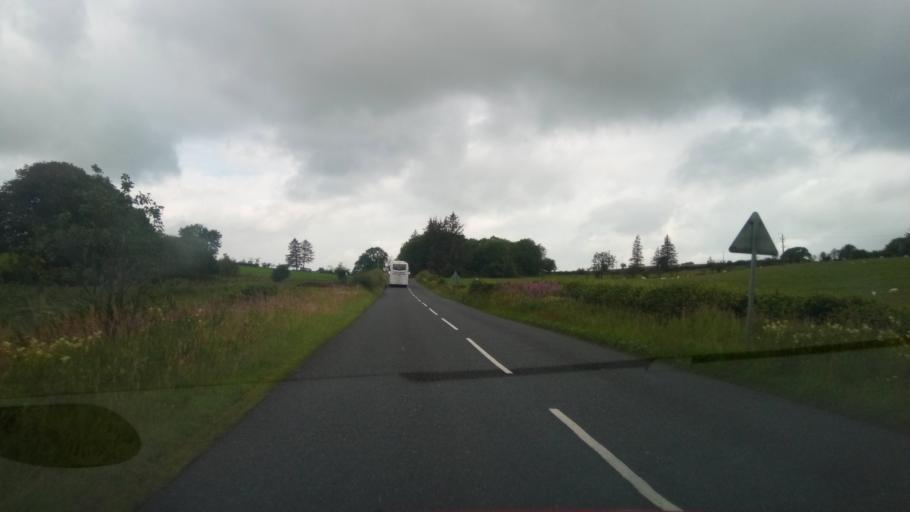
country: GB
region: Scotland
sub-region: Dumfries and Galloway
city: Langholm
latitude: 55.0907
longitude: -2.9176
